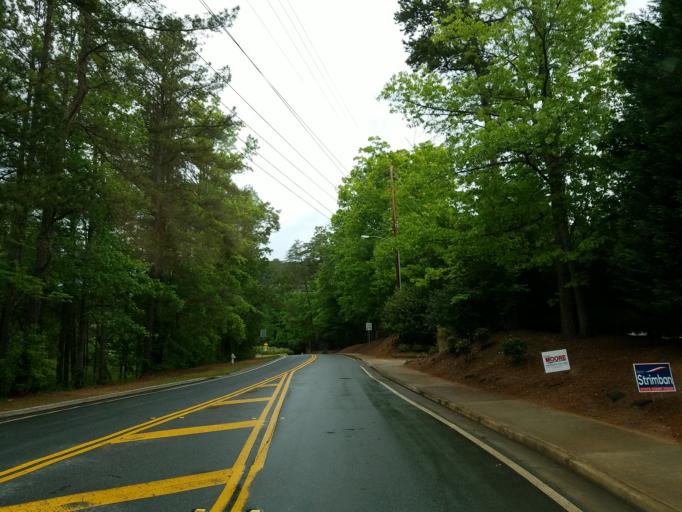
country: US
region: Georgia
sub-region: Fulton County
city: Roswell
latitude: 33.9904
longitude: -84.4429
